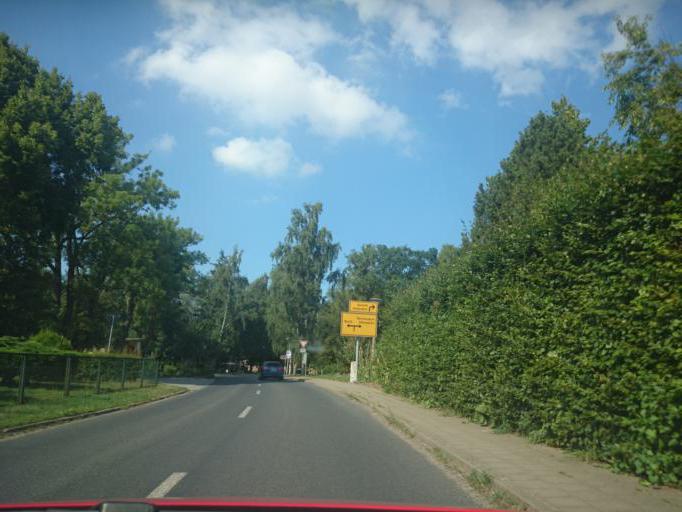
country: DE
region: Mecklenburg-Vorpommern
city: Velgast
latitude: 54.3318
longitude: 12.7969
